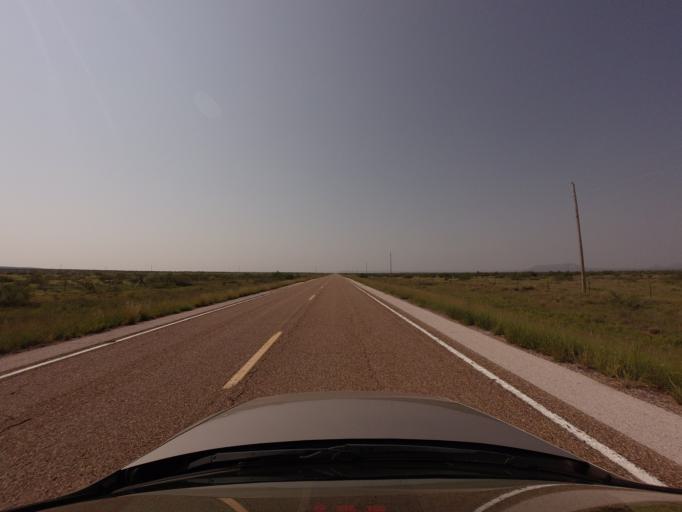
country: US
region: New Mexico
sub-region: Quay County
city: Tucumcari
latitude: 35.0008
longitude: -103.7437
